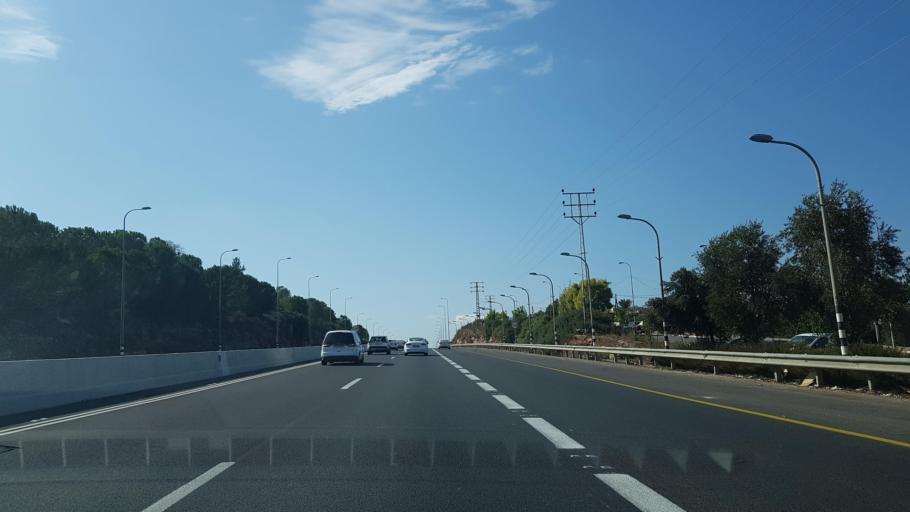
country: IL
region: Northern District
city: Rumat Heib
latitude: 32.7677
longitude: 35.3099
